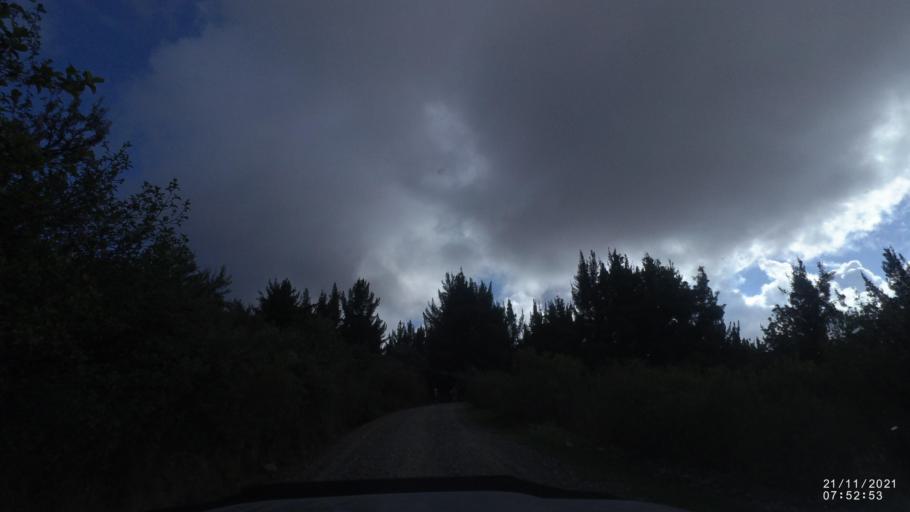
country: BO
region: Cochabamba
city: Cochabamba
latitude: -17.3038
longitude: -66.2185
